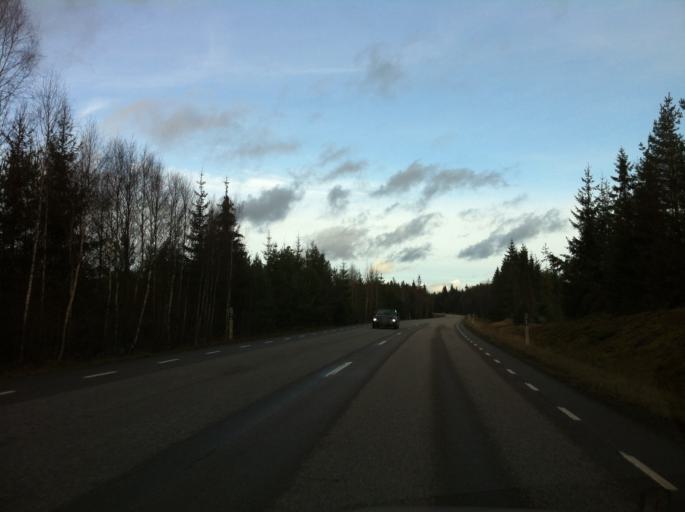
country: SE
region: Kronoberg
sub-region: Almhults Kommun
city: AElmhult
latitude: 56.5577
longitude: 14.1781
